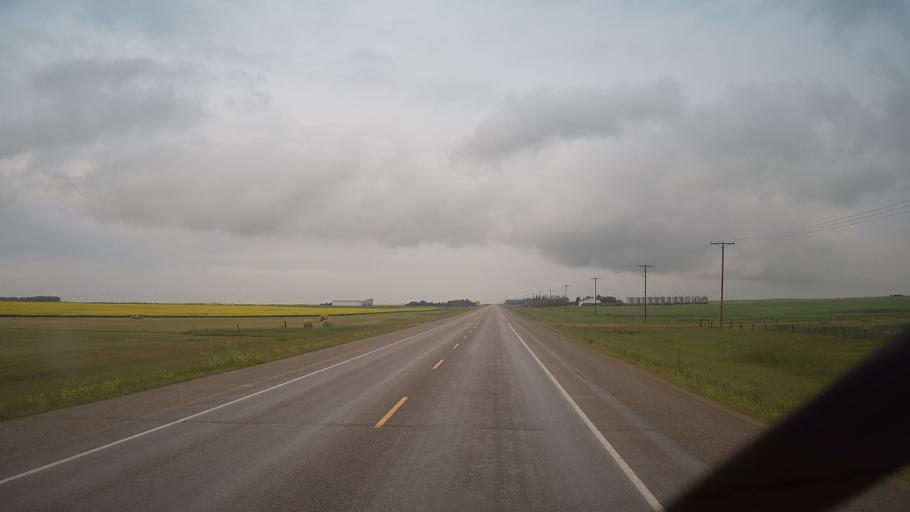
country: CA
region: Saskatchewan
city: Wilkie
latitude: 52.4056
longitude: -108.7602
